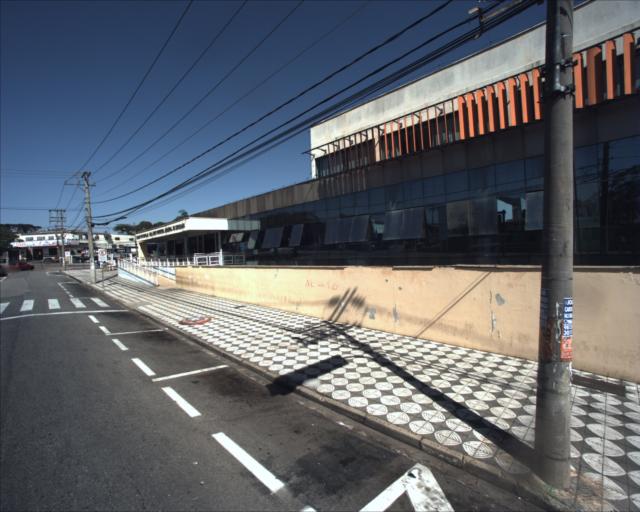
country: BR
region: Sao Paulo
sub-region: Sorocaba
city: Sorocaba
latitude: -23.4832
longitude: -47.4721
